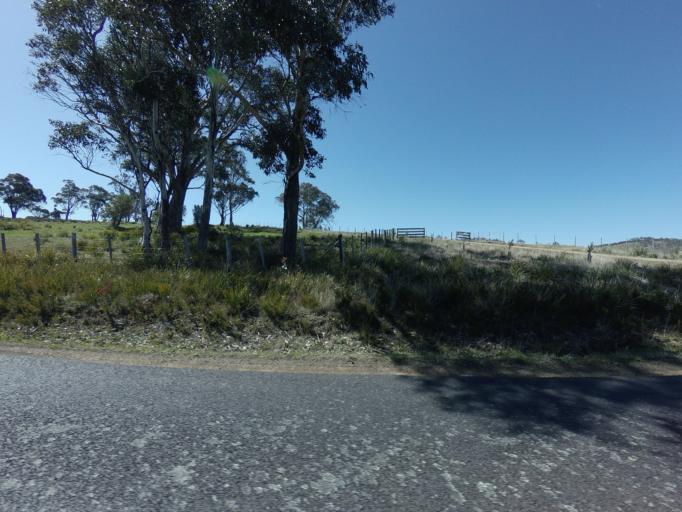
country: AU
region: Tasmania
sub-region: Derwent Valley
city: New Norfolk
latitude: -42.6315
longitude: 146.7345
